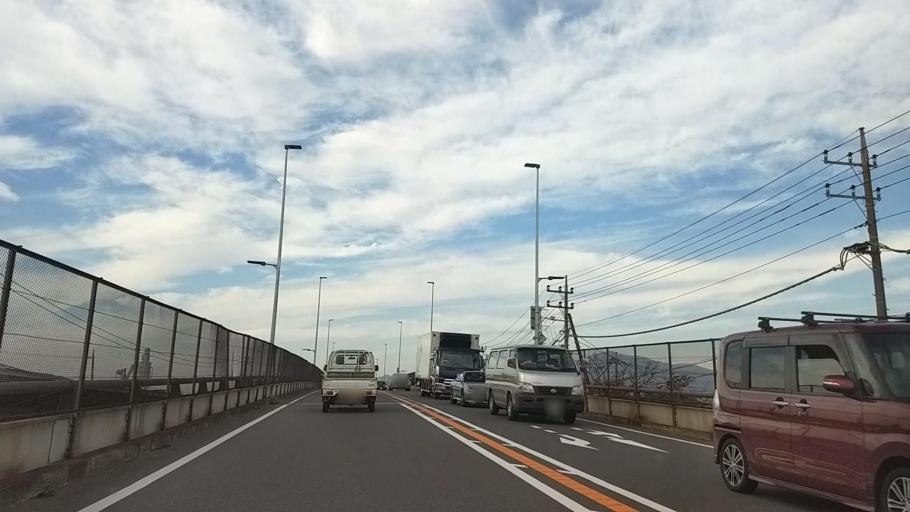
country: JP
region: Kanagawa
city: Atsugi
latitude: 35.4064
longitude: 139.3820
